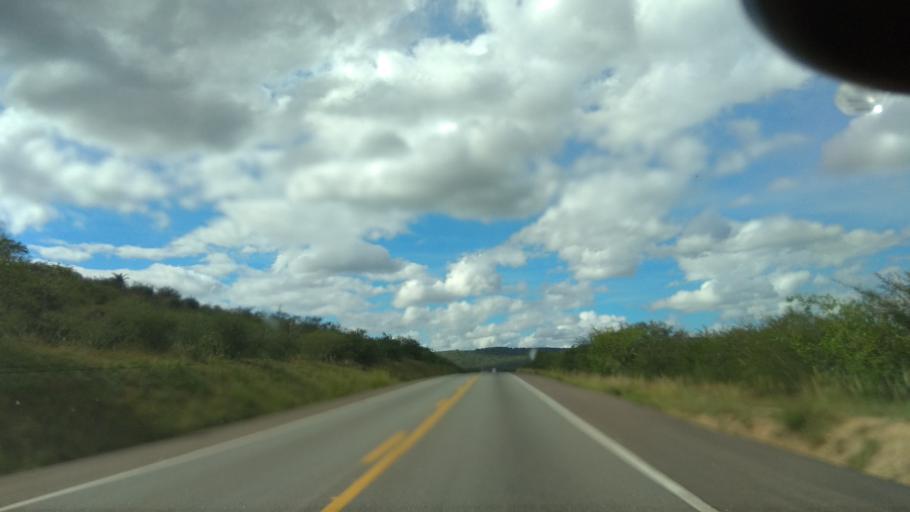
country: BR
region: Bahia
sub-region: Amargosa
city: Amargosa
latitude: -12.9280
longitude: -39.8833
